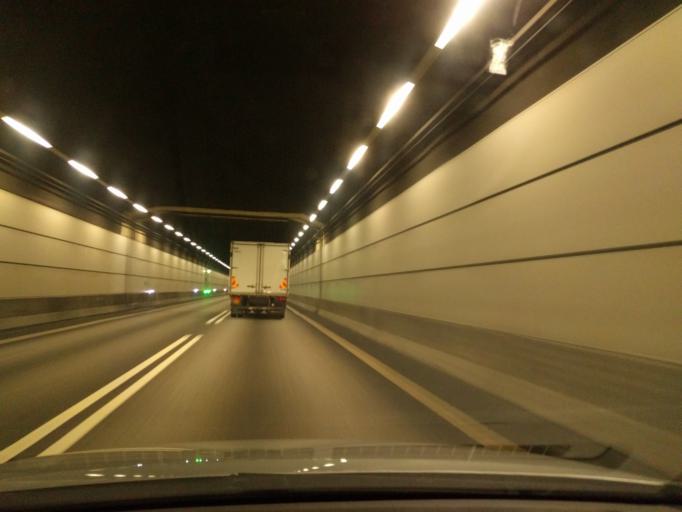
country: DK
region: Capital Region
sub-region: Dragor Kommune
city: Dragor
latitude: 55.6246
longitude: 12.6947
